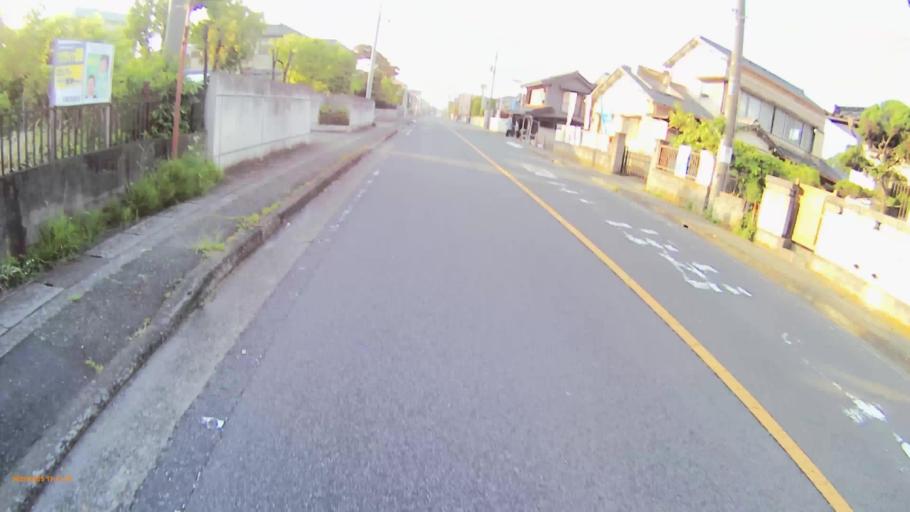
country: JP
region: Saitama
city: Kurihashi
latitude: 36.1359
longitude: 139.7052
